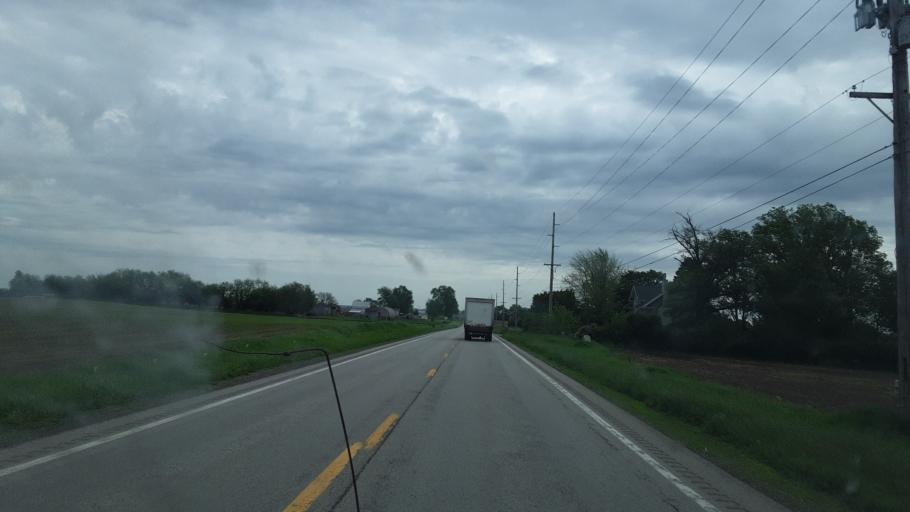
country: US
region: Illinois
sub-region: Tazewell County
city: Delavan
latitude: 40.3056
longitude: -89.5929
